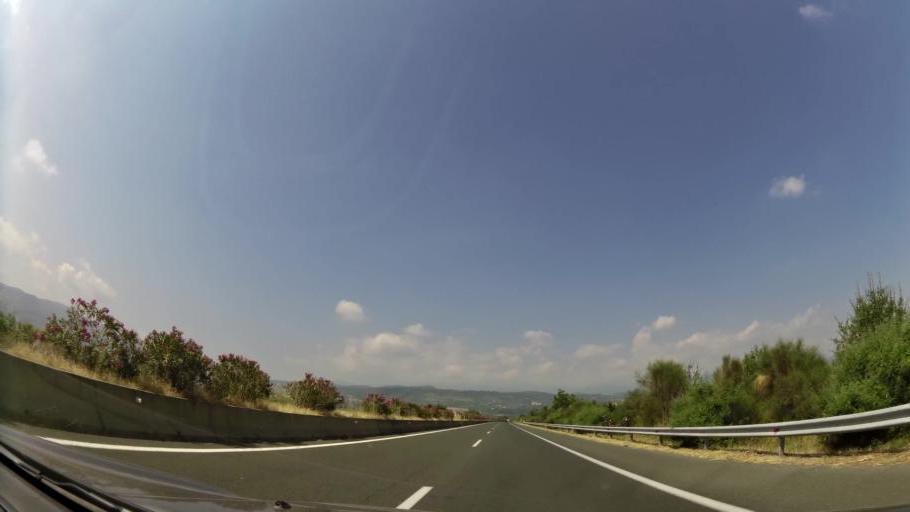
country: GR
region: Central Macedonia
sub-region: Nomos Imathias
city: Diavatos
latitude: 40.5213
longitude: 22.2658
